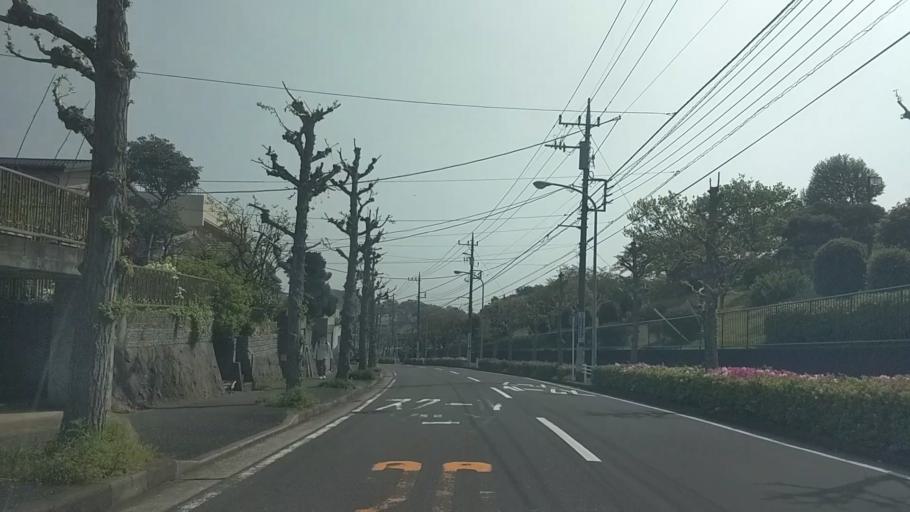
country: JP
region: Kanagawa
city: Zushi
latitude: 35.3642
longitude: 139.6194
